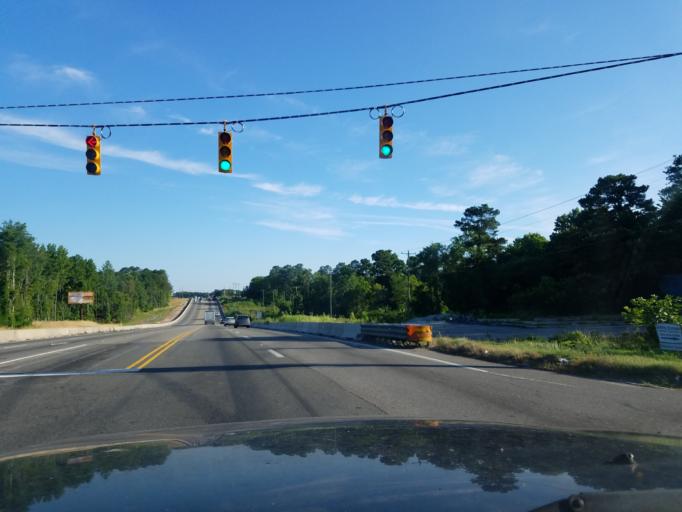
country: US
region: North Carolina
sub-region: Durham County
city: Durham
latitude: 35.9657
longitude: -78.8468
